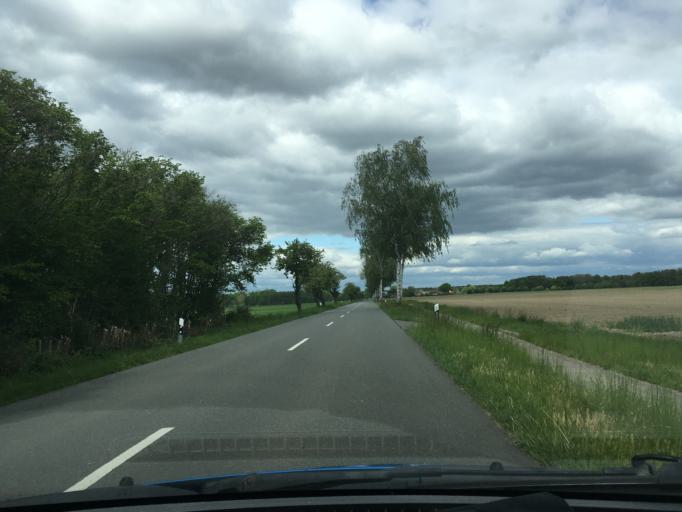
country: DE
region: Lower Saxony
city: Suderburg
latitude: 52.9118
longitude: 10.4215
